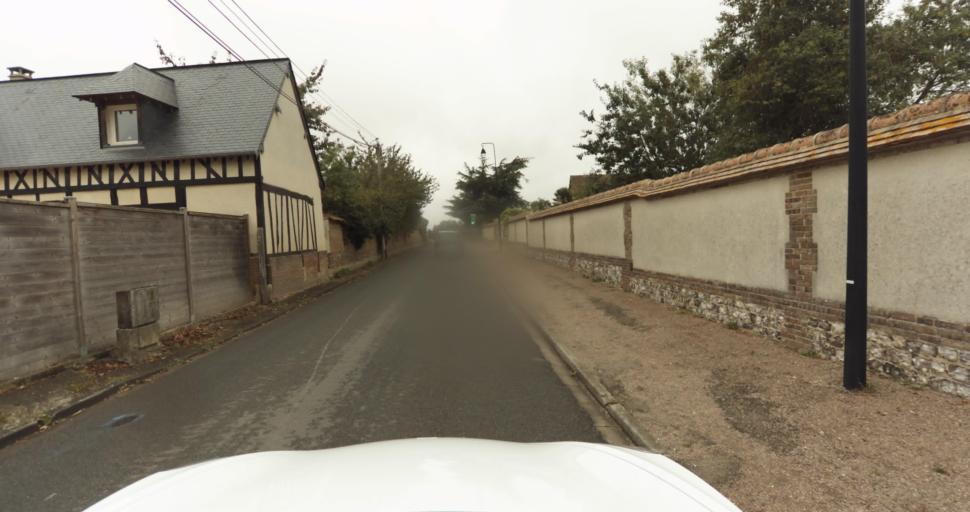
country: FR
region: Haute-Normandie
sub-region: Departement de l'Eure
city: Aviron
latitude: 49.0806
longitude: 1.0771
